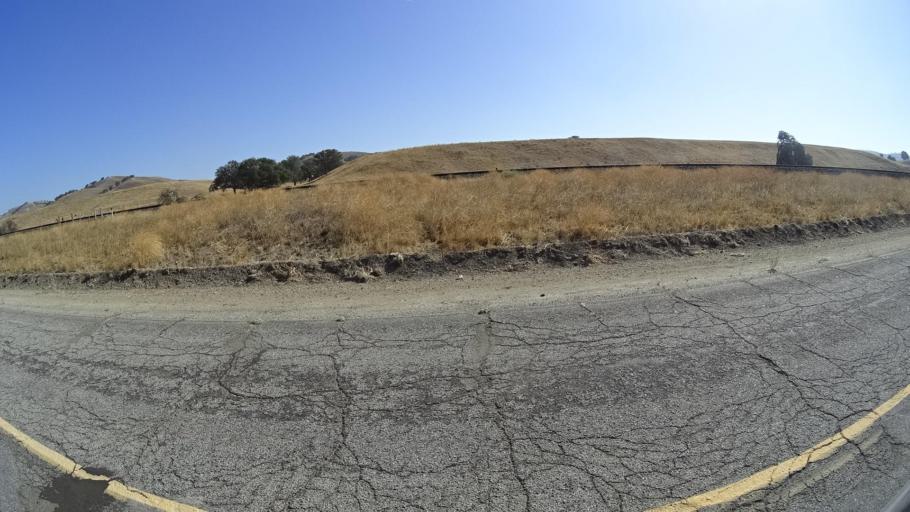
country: US
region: California
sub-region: San Luis Obispo County
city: San Miguel
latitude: 35.8460
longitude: -120.7537
